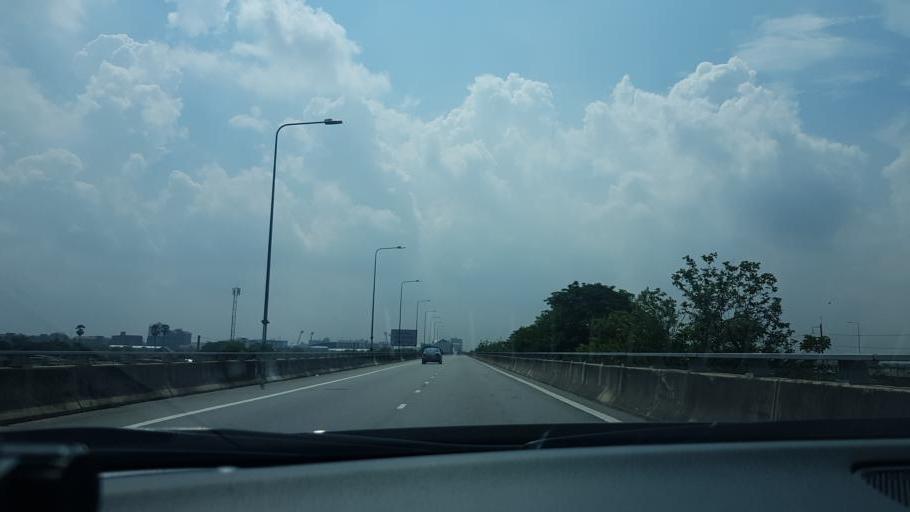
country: TH
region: Pathum Thani
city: Khlong Luang
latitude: 14.0663
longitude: 100.5851
